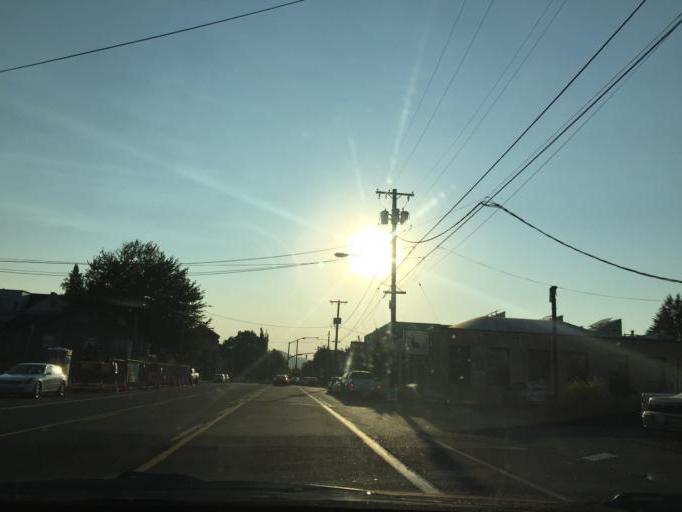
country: US
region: Oregon
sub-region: Multnomah County
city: Portland
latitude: 45.5265
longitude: -122.6419
